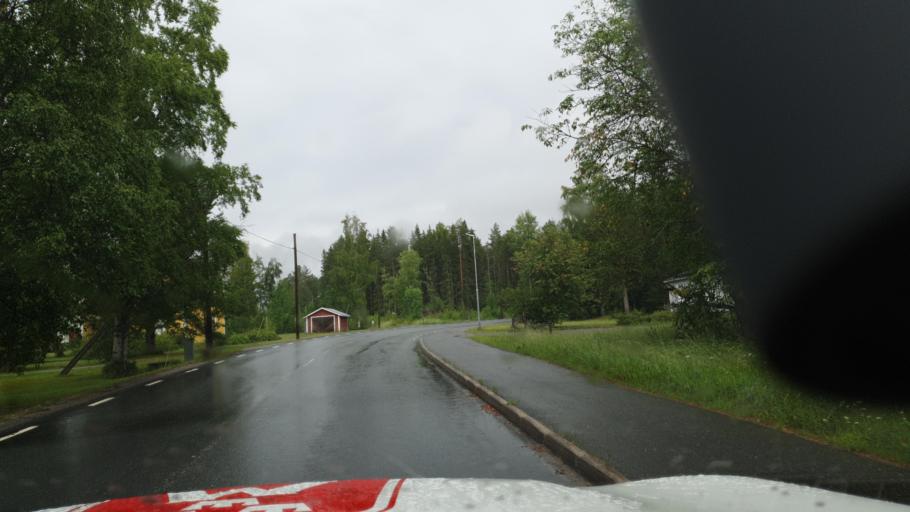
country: SE
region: Vaesterbotten
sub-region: Nordmalings Kommun
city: Nordmaling
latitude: 63.5760
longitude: 19.5263
